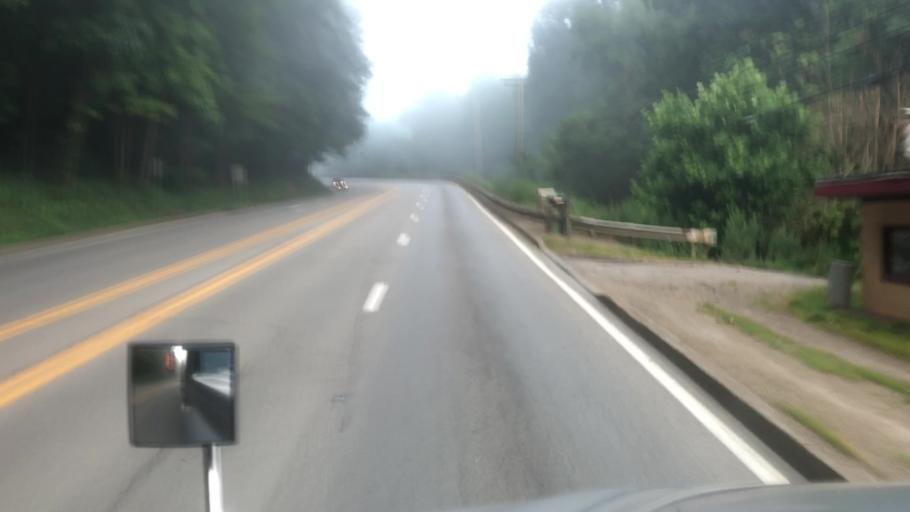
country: US
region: Pennsylvania
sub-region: Venango County
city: Franklin
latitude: 41.3884
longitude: -79.8430
